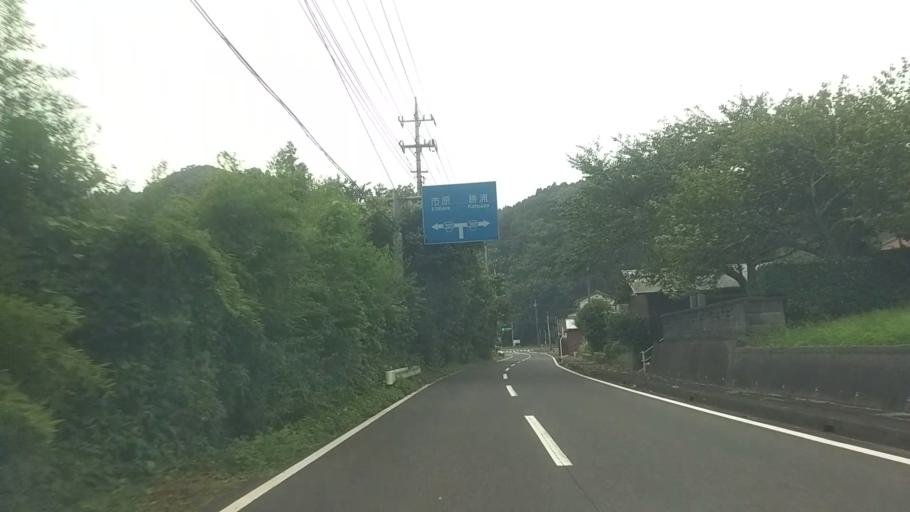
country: JP
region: Chiba
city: Ohara
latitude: 35.2694
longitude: 140.2543
